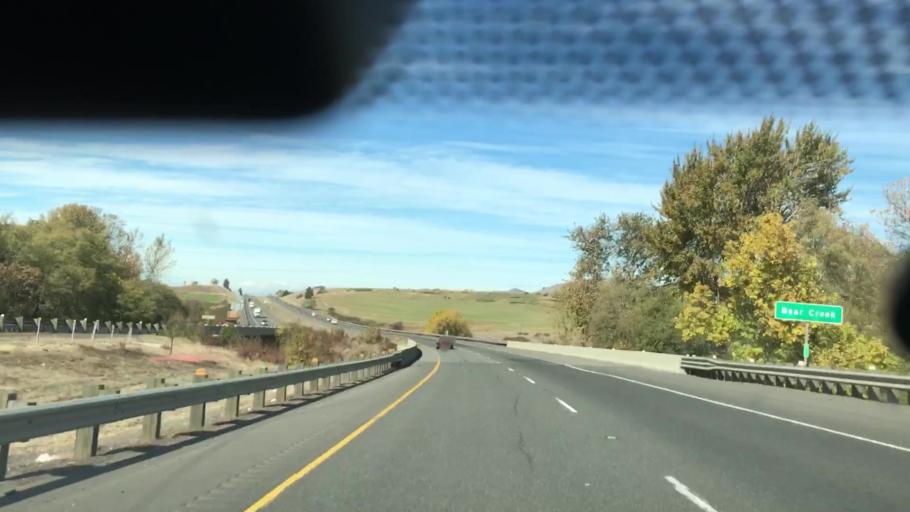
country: US
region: Oregon
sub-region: Jackson County
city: Ashland
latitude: 42.1948
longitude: -122.6724
